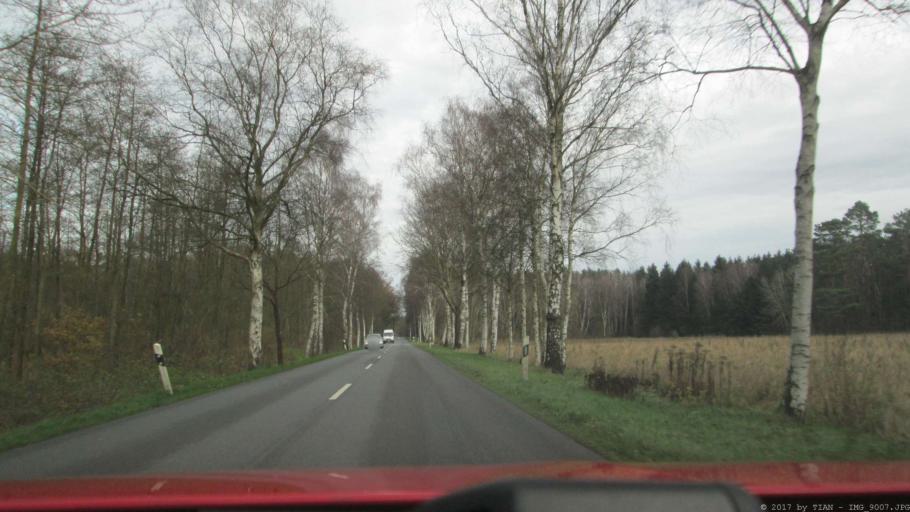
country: DE
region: Lower Saxony
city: Schoneworde
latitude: 52.6379
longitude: 10.6955
